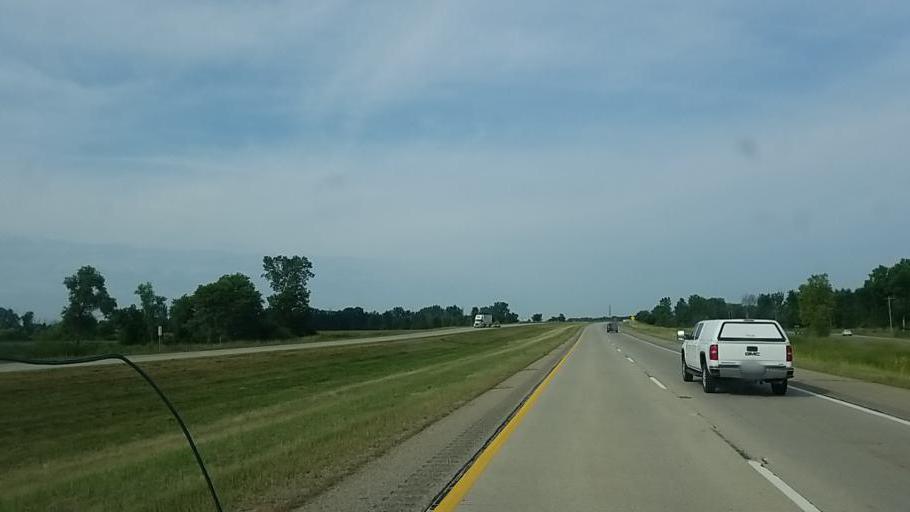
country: US
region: Michigan
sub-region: Eaton County
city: Potterville
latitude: 42.6090
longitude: -84.7627
